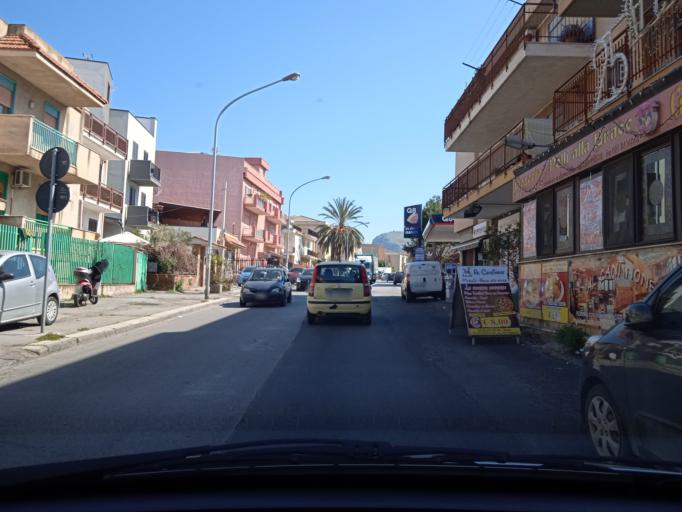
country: IT
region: Sicily
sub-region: Palermo
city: Villabate
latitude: 38.0920
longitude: 13.4313
